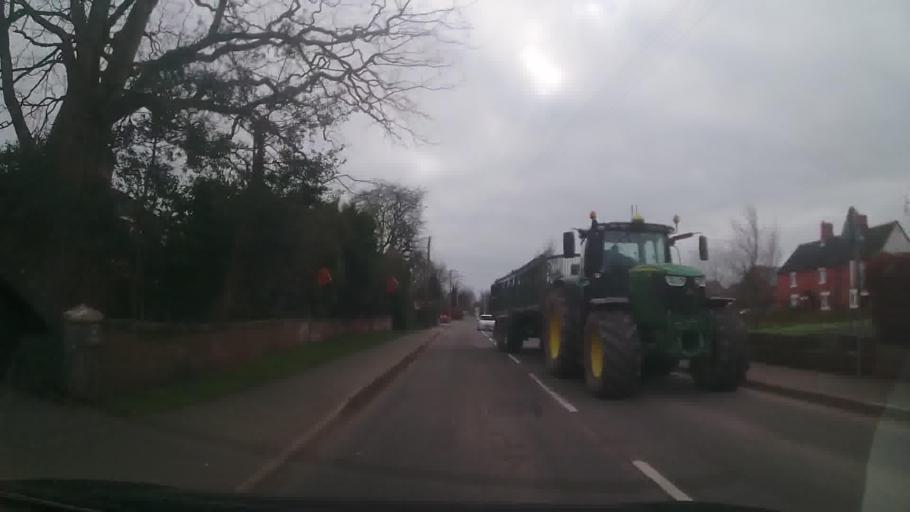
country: GB
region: England
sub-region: Shropshire
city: Great Ness
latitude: 52.7843
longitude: -2.8530
